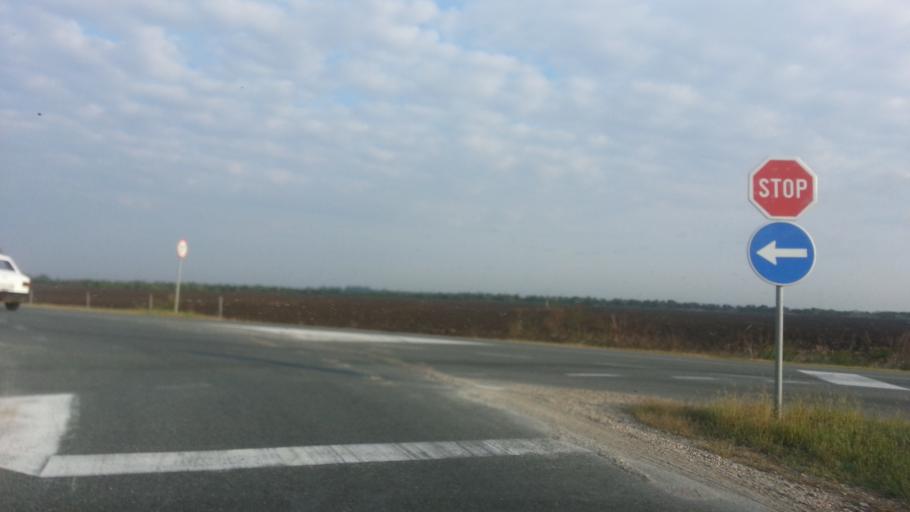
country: RS
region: Autonomna Pokrajina Vojvodina
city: Nova Pazova
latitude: 44.9865
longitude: 20.2198
